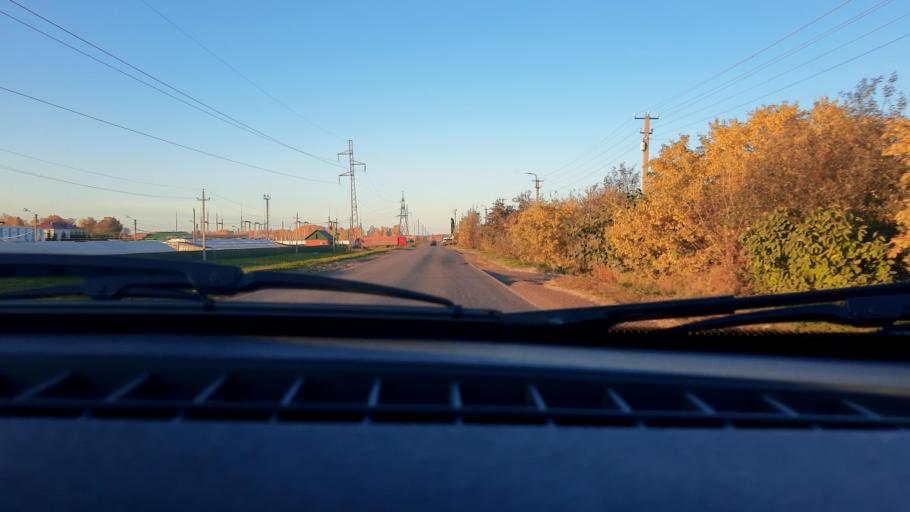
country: RU
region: Bashkortostan
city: Ufa
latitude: 54.8402
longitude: 55.9983
